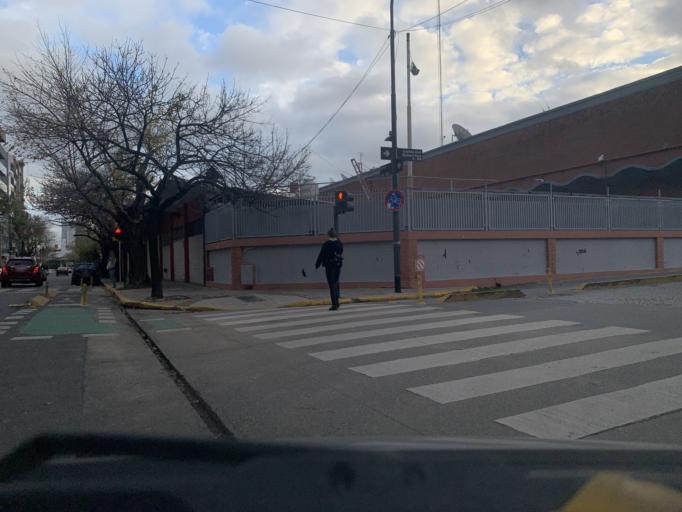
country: AR
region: Buenos Aires F.D.
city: Colegiales
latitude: -34.5806
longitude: -58.4421
